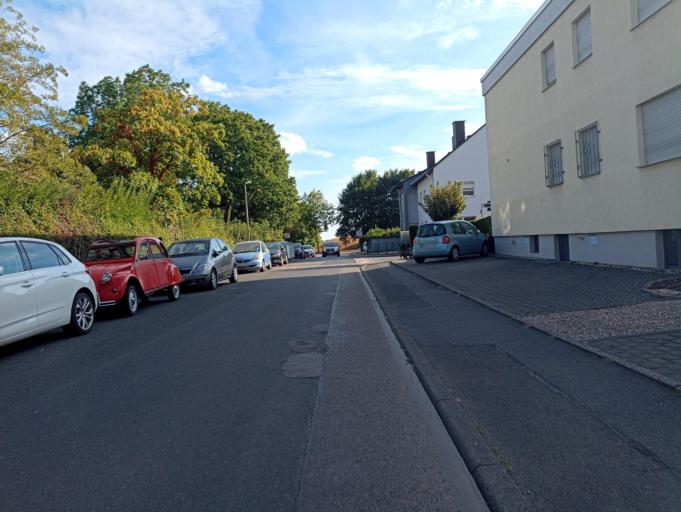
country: DE
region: Hesse
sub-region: Regierungsbezirk Darmstadt
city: Bad Homburg vor der Hoehe
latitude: 50.2149
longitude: 8.6309
